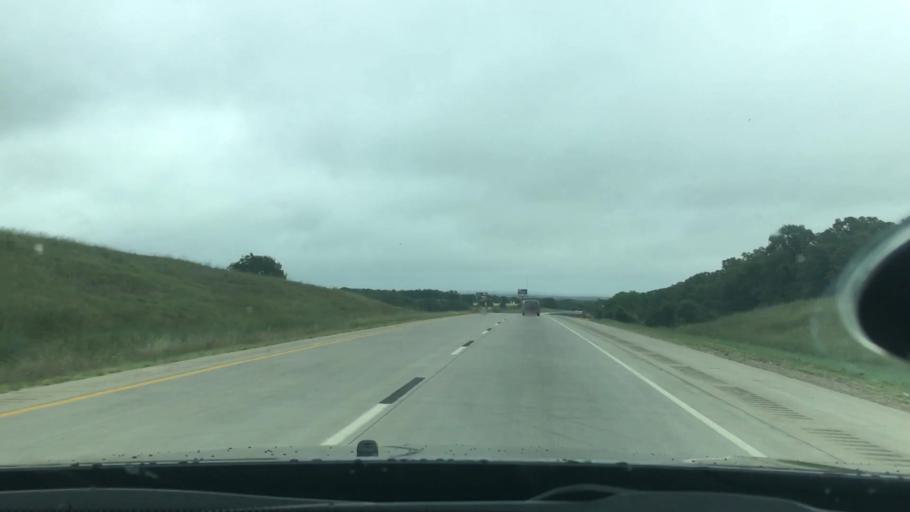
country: US
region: Oklahoma
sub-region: Okfuskee County
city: Boley
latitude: 35.3841
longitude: -96.5080
